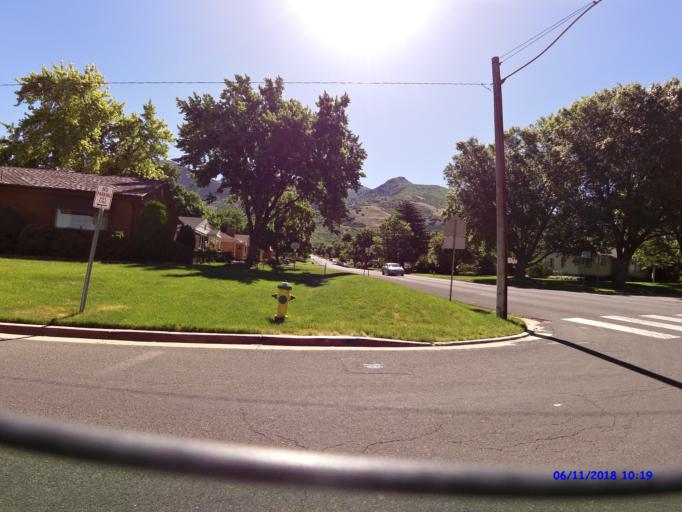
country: US
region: Utah
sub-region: Weber County
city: South Ogden
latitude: 41.1976
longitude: -111.9460
